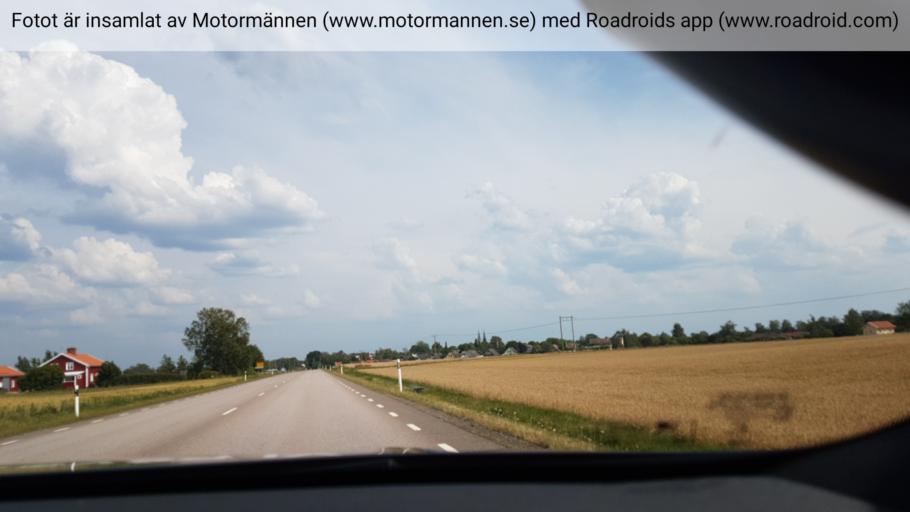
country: SE
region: Vaestra Goetaland
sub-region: Skara Kommun
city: Skara
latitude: 58.3956
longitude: 13.4150
